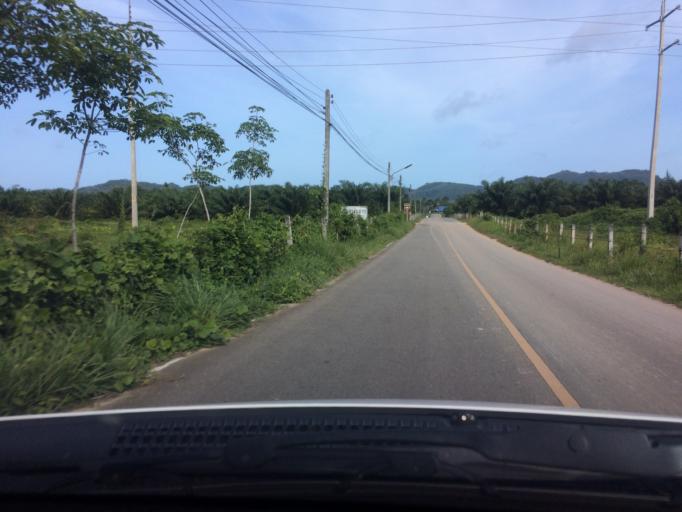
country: TH
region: Phuket
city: Thalang
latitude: 8.0433
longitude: 98.3337
